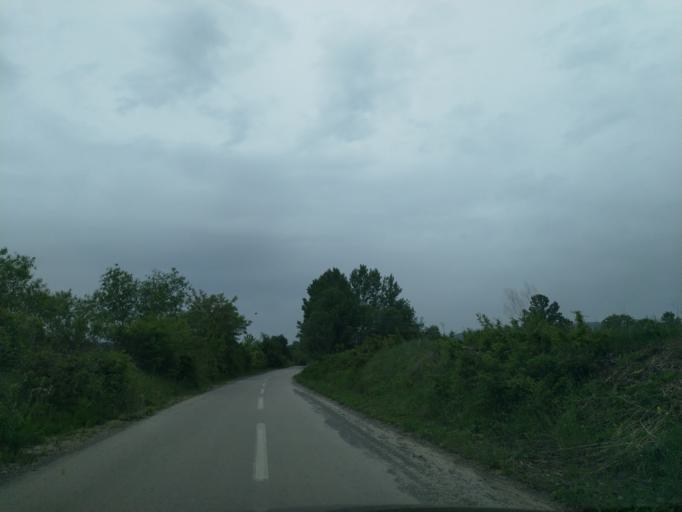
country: RS
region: Central Serbia
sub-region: Pomoravski Okrug
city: Paracin
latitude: 43.8680
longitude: 21.5735
